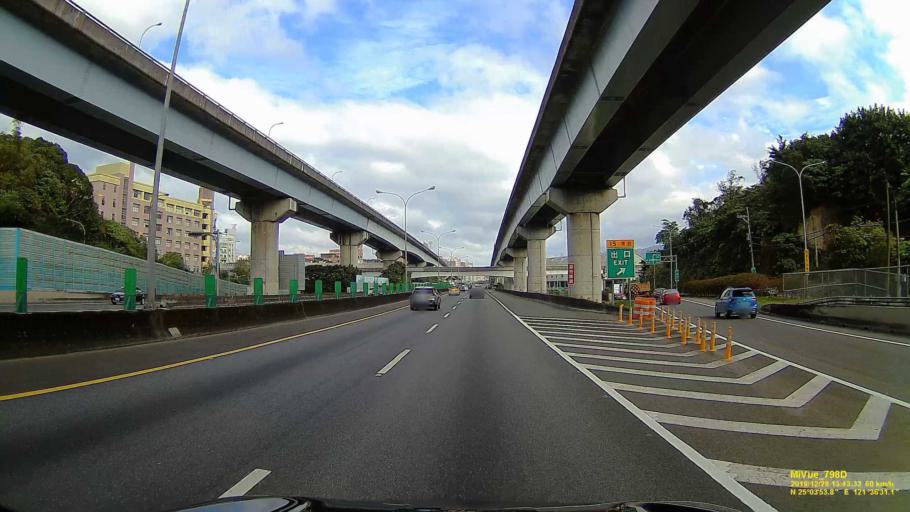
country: TW
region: Taipei
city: Taipei
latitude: 25.0650
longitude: 121.6090
